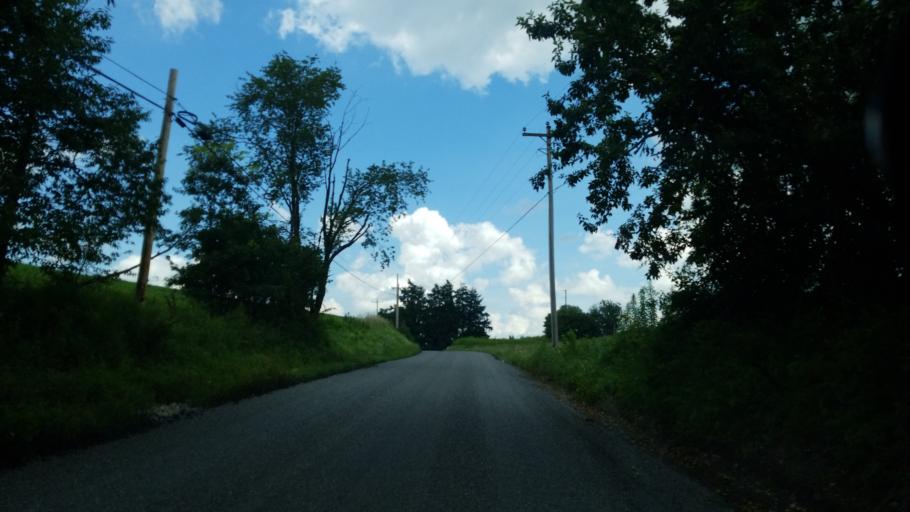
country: US
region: Pennsylvania
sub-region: Jefferson County
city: Brookville
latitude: 41.2311
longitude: -79.0035
